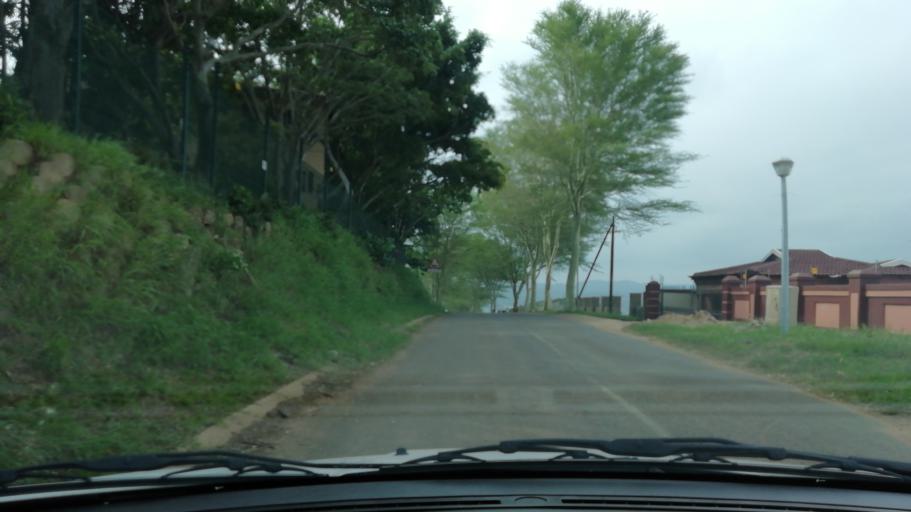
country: ZA
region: KwaZulu-Natal
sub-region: uThungulu District Municipality
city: Empangeni
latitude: -28.7406
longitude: 31.8797
